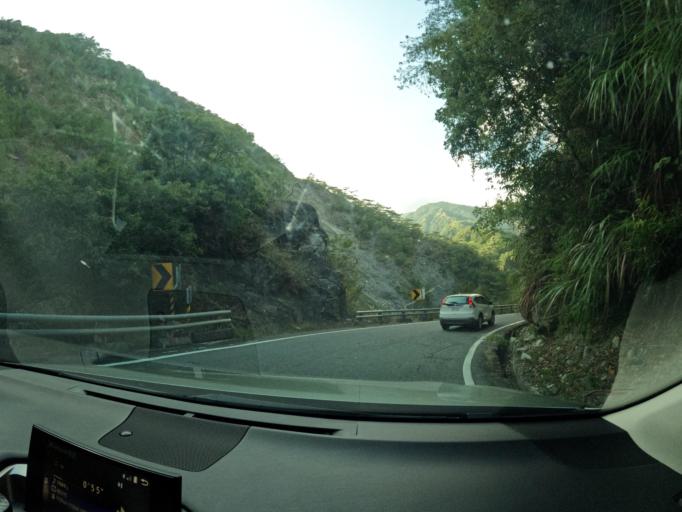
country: TW
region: Taiwan
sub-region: Taitung
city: Taitung
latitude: 23.1817
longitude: 121.0204
